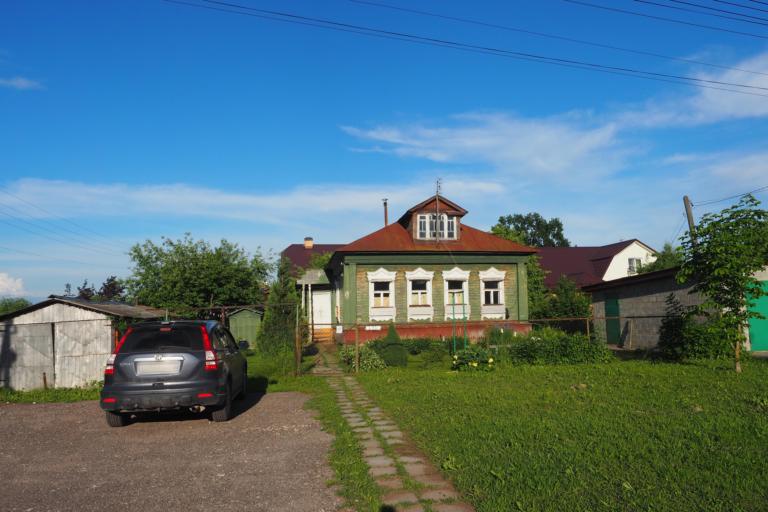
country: RU
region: Moskovskaya
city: Ashitkovo
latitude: 55.4394
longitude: 38.6060
